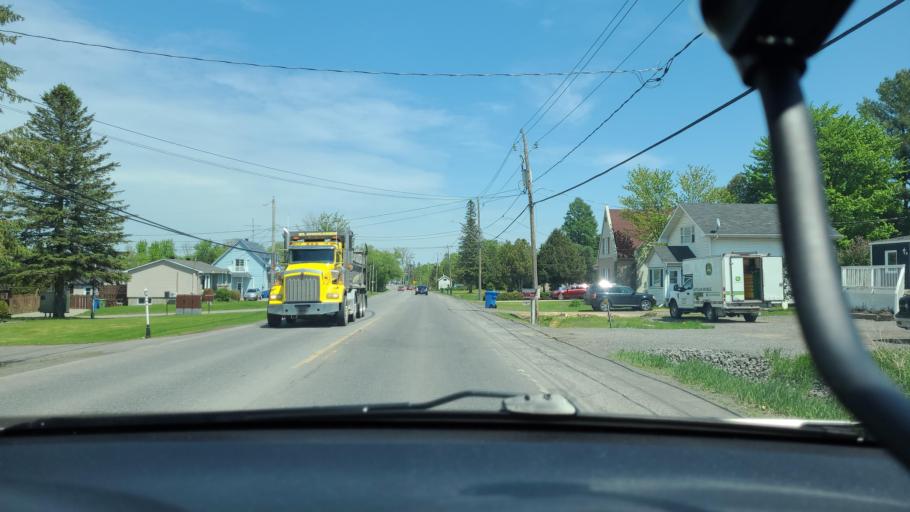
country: CA
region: Quebec
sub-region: Laurentides
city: Lachute
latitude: 45.6609
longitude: -74.3125
